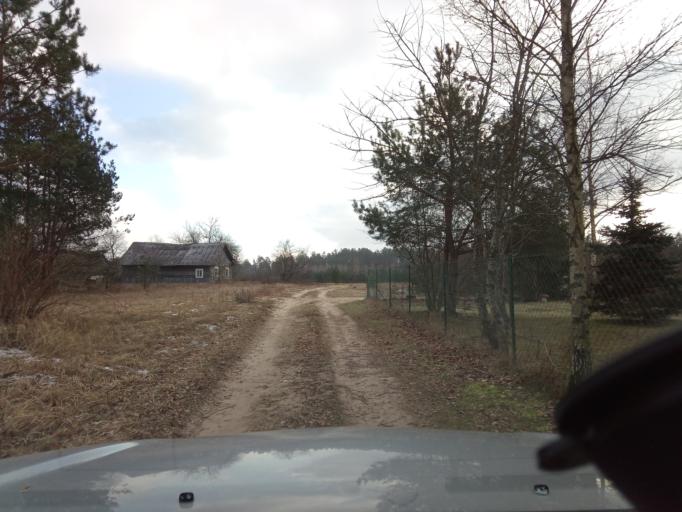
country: LT
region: Alytaus apskritis
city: Druskininkai
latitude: 54.1121
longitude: 24.2199
